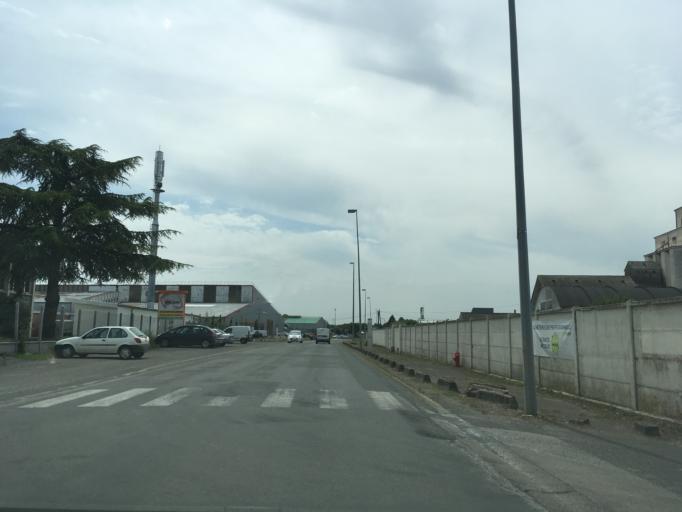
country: FR
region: Poitou-Charentes
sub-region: Departement des Deux-Sevres
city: Niort
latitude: 46.3059
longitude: -0.4603
